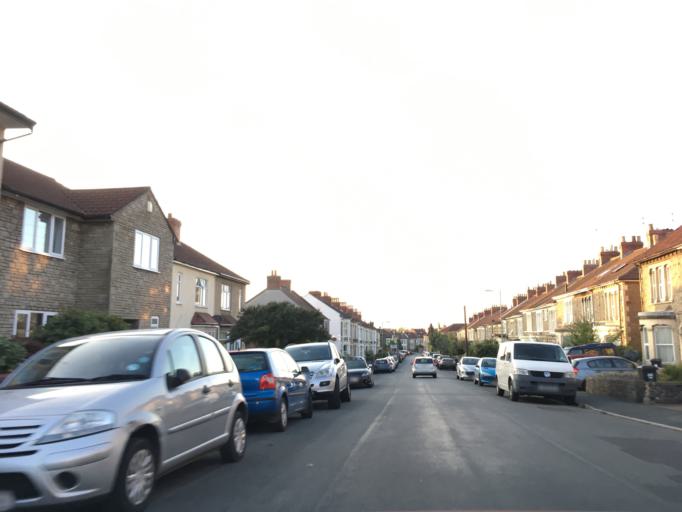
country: GB
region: England
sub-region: South Gloucestershire
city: Mangotsfield
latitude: 51.4827
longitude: -2.5156
